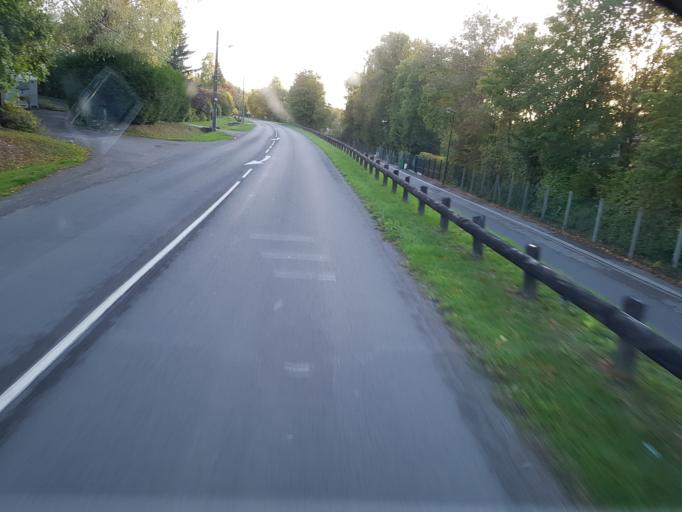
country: FR
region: Picardie
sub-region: Departement de la Somme
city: Salouel
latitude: 49.8657
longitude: 2.2471
